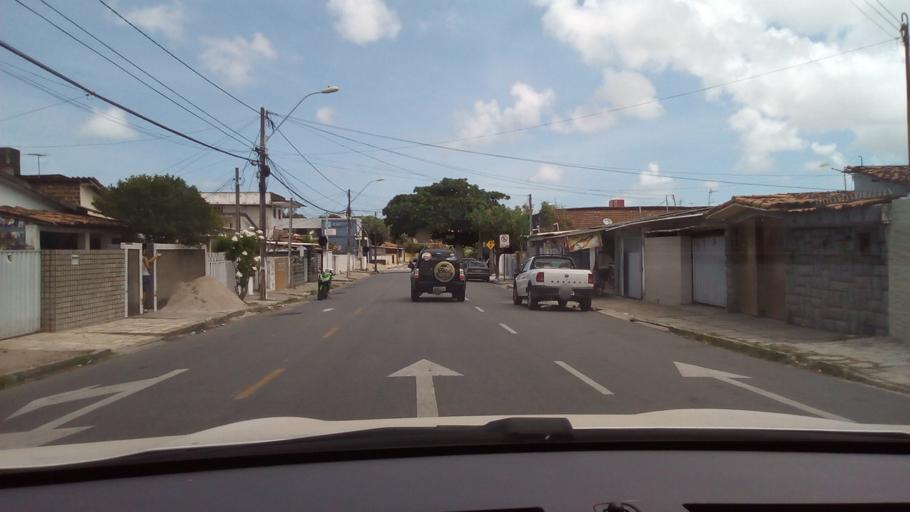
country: BR
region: Paraiba
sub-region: Joao Pessoa
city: Joao Pessoa
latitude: -7.1252
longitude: -34.8610
